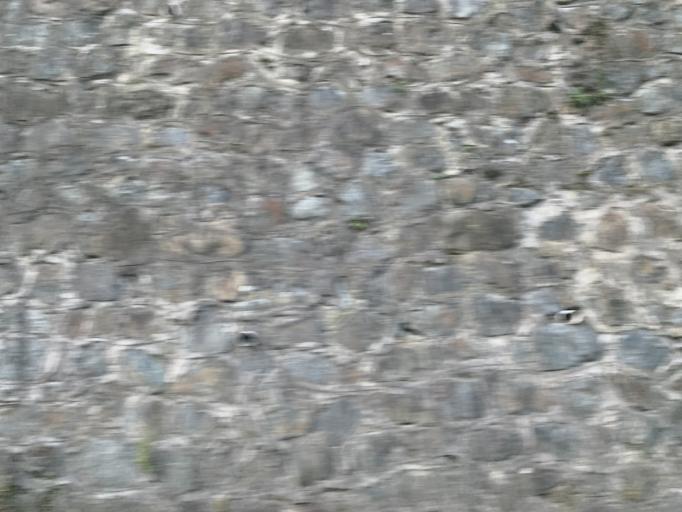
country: TR
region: Trabzon
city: Of
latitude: 40.8754
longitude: 40.2797
